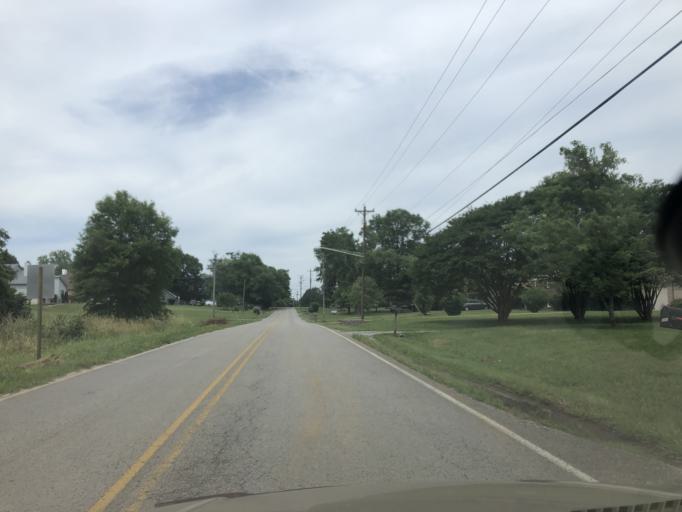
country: US
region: Tennessee
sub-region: Davidson County
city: Lakewood
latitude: 36.2577
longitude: -86.6122
